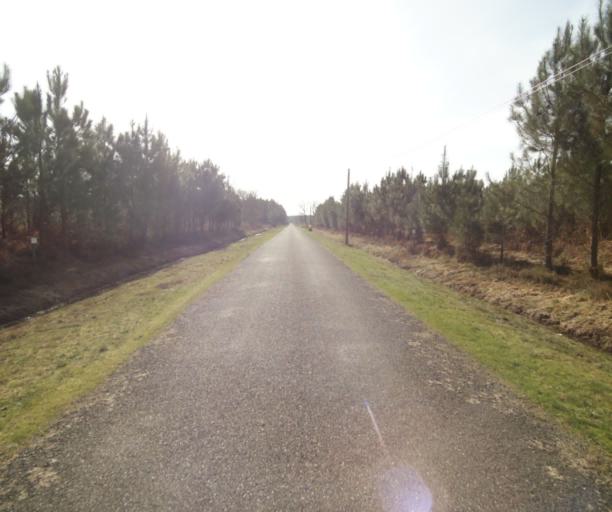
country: FR
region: Aquitaine
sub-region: Departement des Landes
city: Roquefort
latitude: 44.1431
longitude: -0.1777
